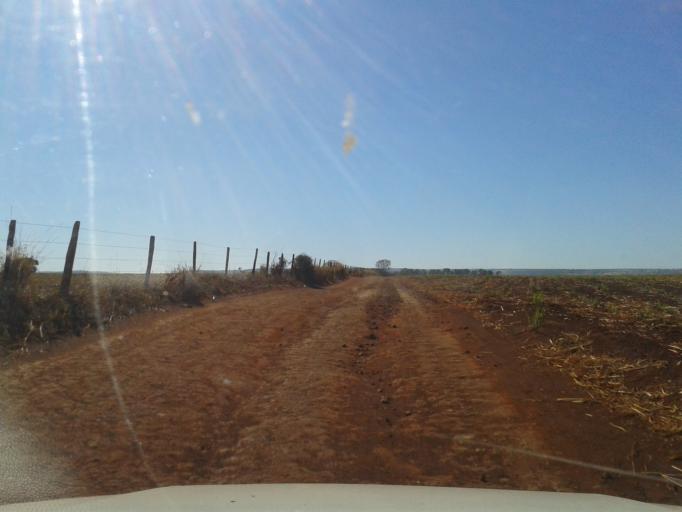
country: BR
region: Minas Gerais
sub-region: Centralina
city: Centralina
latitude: -18.5906
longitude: -49.1639
